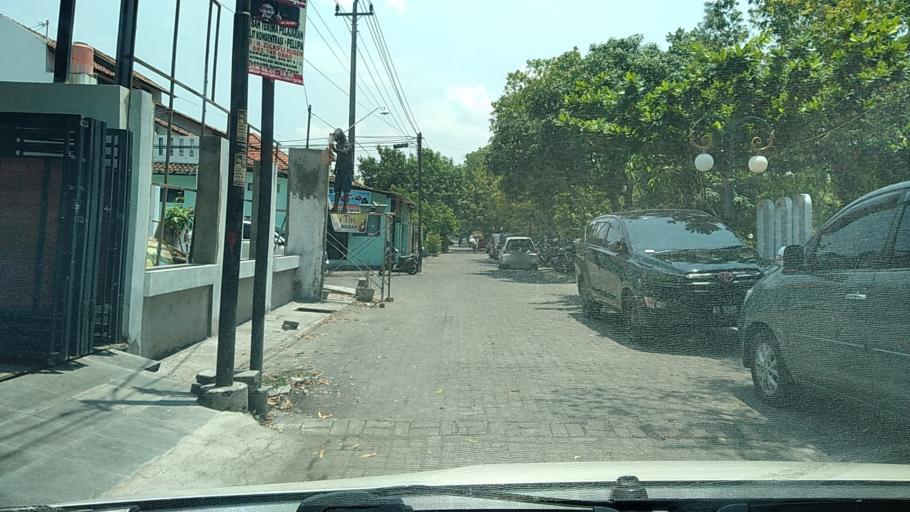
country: ID
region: Central Java
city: Semarang
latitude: -6.9809
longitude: 110.3894
